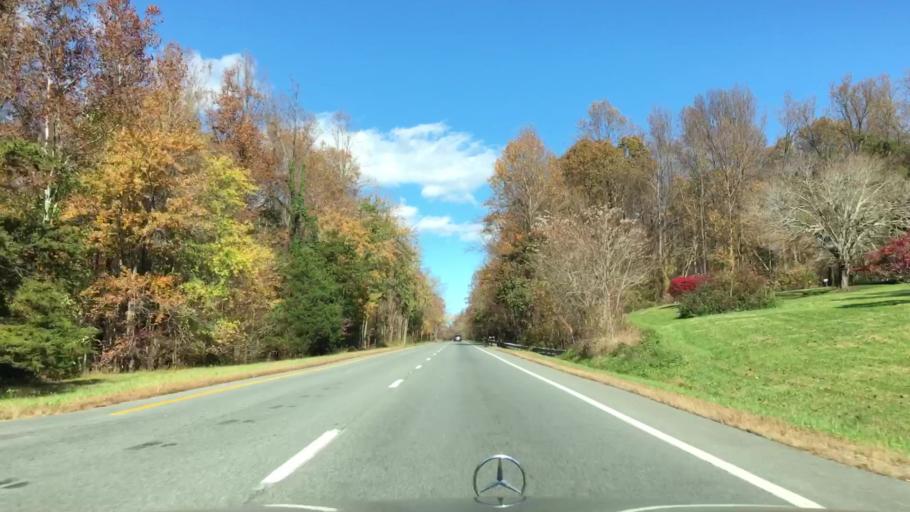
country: US
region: Virginia
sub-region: Albemarle County
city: Crozet
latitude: 37.9377
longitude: -78.6698
